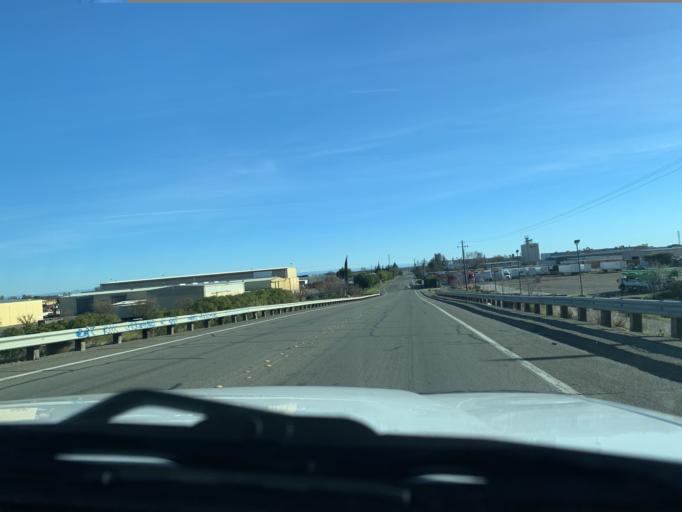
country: US
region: California
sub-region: Yolo County
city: Woodland
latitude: 38.6918
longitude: -121.7549
